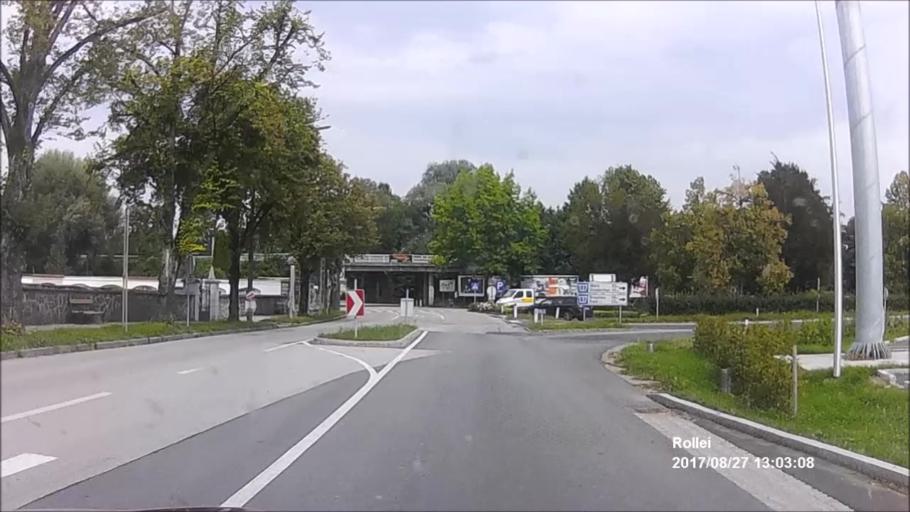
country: AT
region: Upper Austria
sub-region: Politischer Bezirk Scharding
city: Scharding
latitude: 48.4611
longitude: 13.4334
